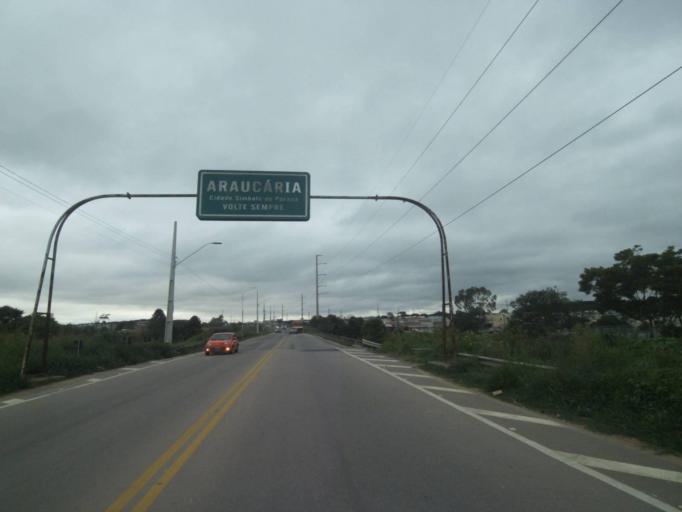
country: BR
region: Parana
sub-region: Araucaria
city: Araucaria
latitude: -25.5272
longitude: -49.3408
